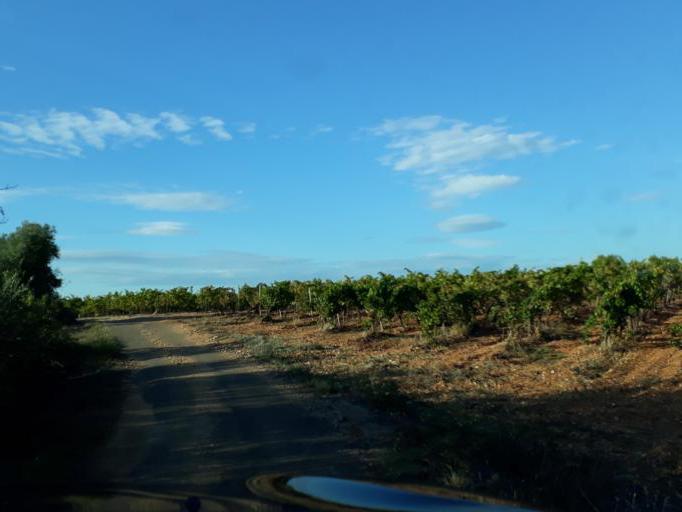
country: FR
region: Languedoc-Roussillon
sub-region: Departement de l'Herault
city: Florensac
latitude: 43.4205
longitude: 3.4735
